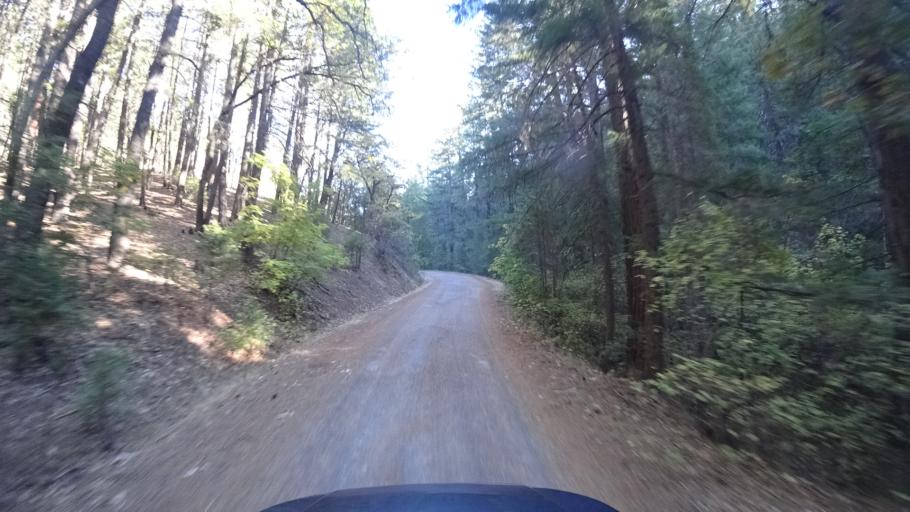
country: US
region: California
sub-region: Trinity County
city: Weaverville
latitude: 41.1498
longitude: -123.1339
